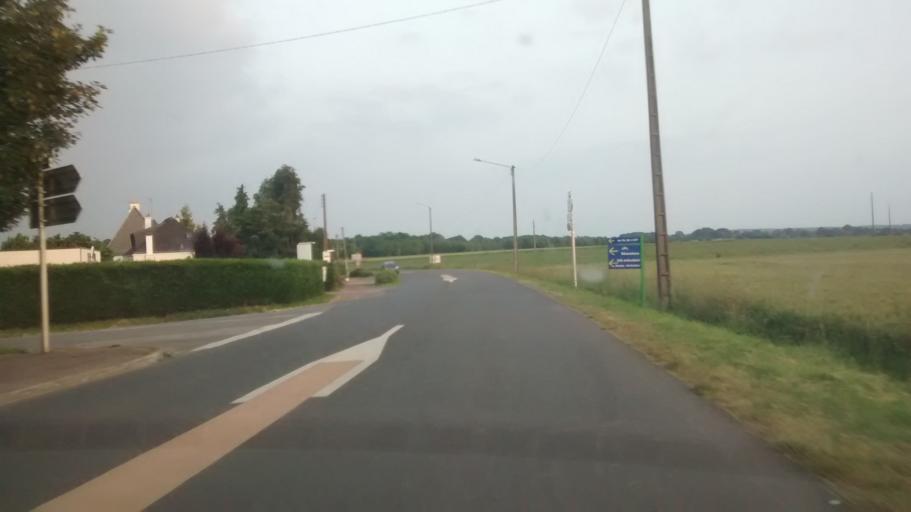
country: FR
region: Brittany
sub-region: Departement du Morbihan
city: Guer
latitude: 47.9358
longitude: -2.1302
